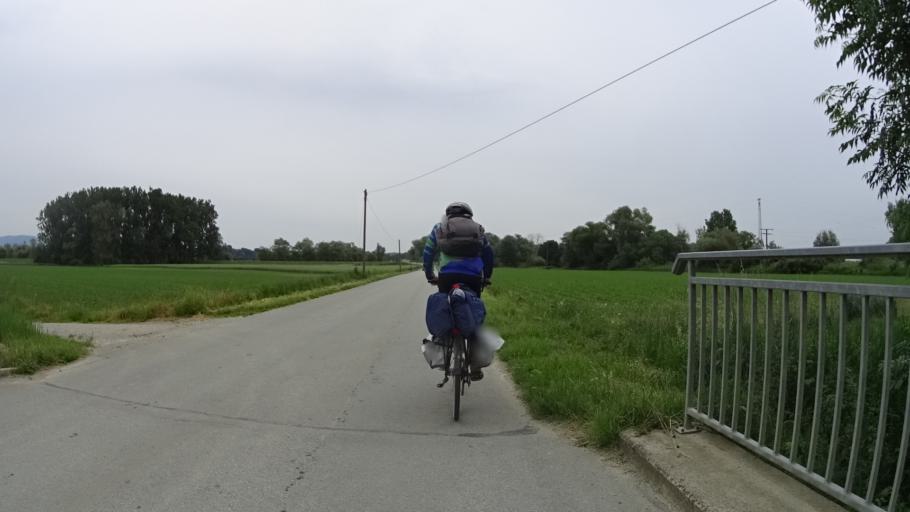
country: DE
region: Bavaria
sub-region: Lower Bavaria
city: Winzer
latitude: 48.7291
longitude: 13.0499
